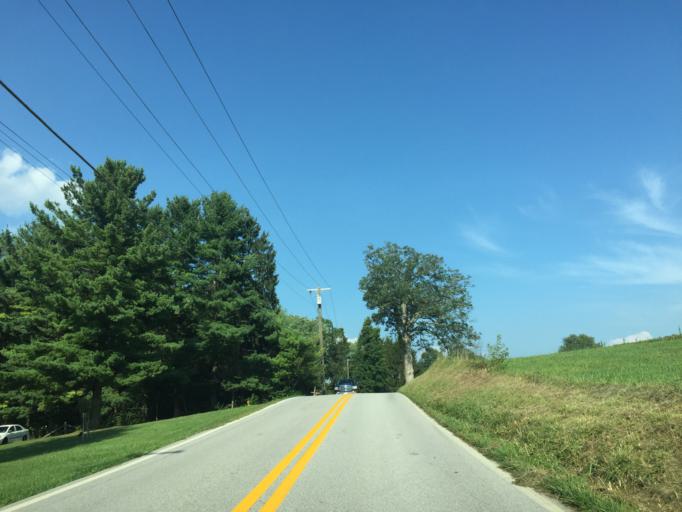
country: US
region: Maryland
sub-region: Carroll County
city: Manchester
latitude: 39.6510
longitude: -76.8427
